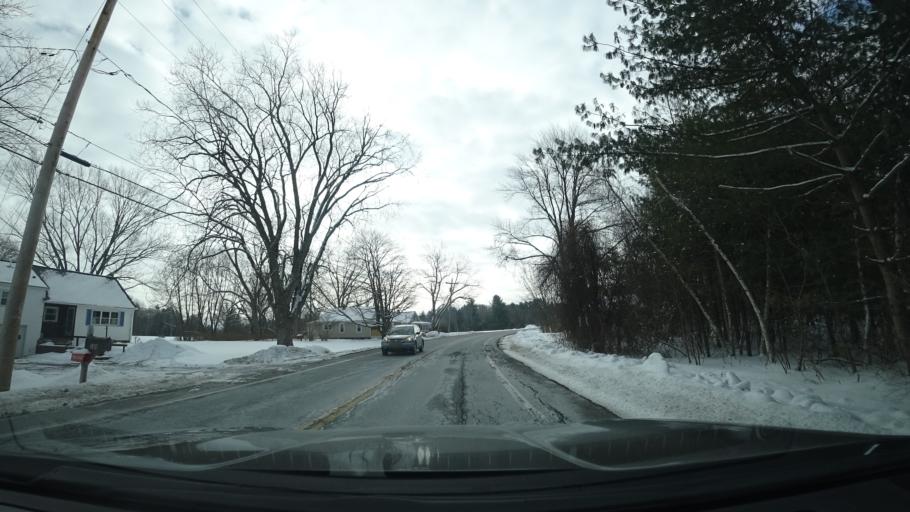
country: US
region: New York
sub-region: Washington County
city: Fort Edward
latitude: 43.2768
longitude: -73.6096
